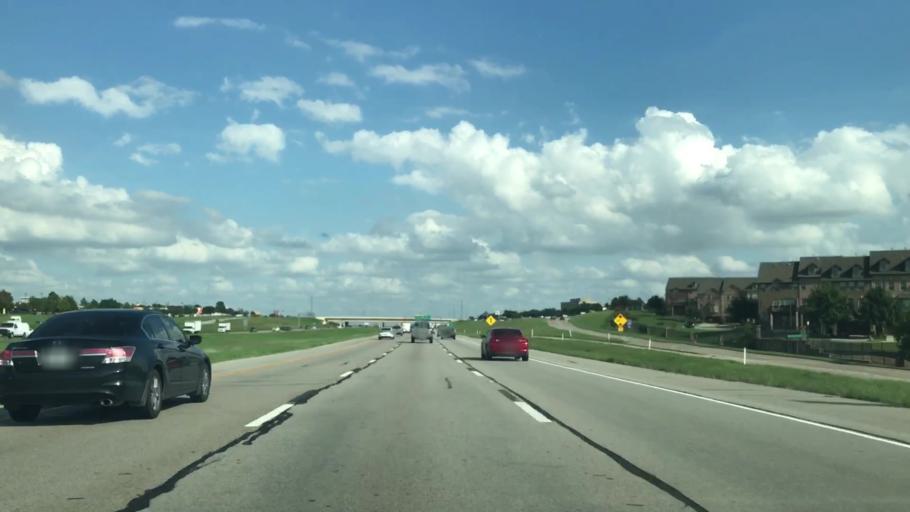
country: US
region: Texas
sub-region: Dallas County
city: Coppell
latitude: 32.9170
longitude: -96.9677
